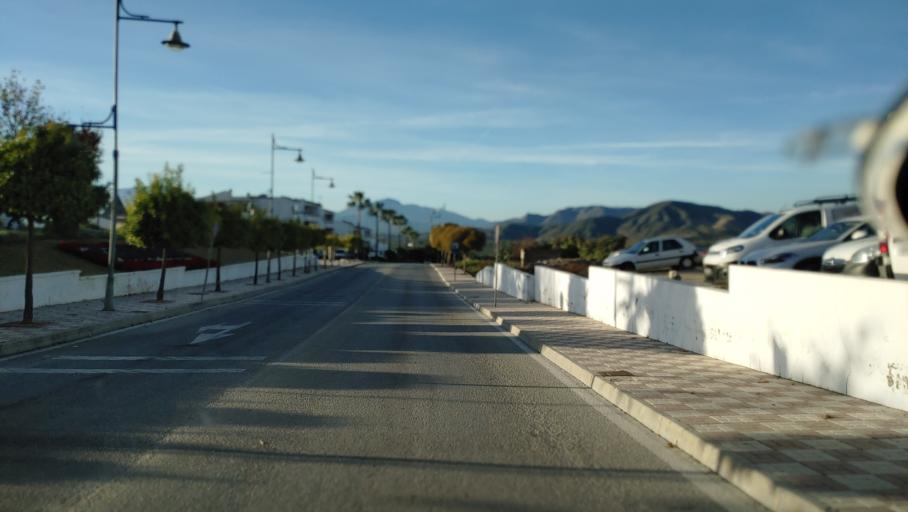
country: ES
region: Andalusia
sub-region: Provincia de Malaga
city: Cartama
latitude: 36.7102
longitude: -4.6343
